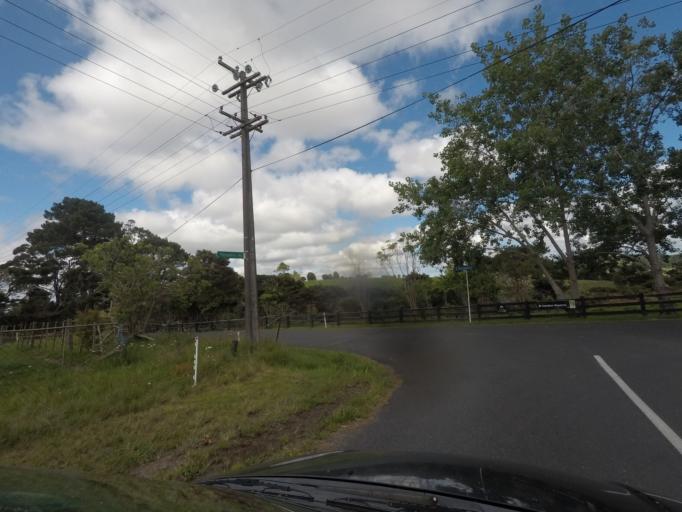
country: NZ
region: Auckland
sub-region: Auckland
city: Rothesay Bay
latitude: -36.7653
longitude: 174.6411
